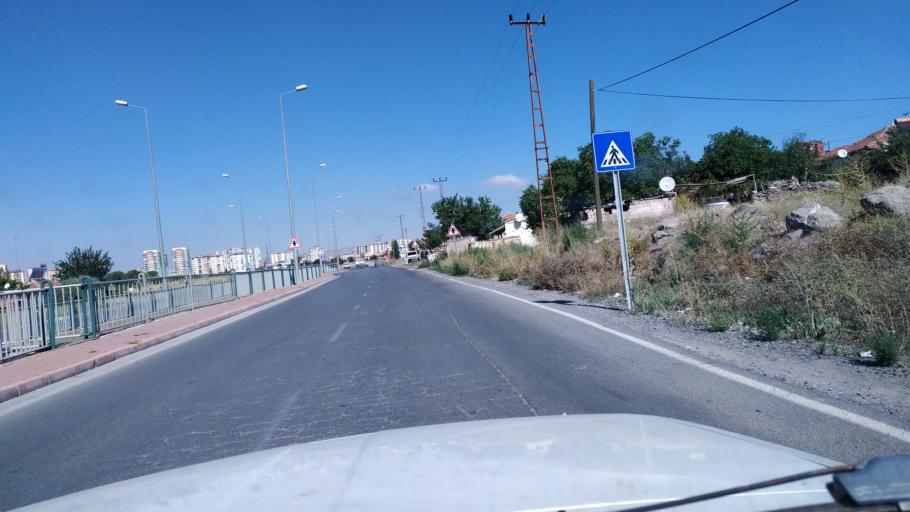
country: TR
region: Kayseri
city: Talas
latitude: 38.7333
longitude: 35.5488
